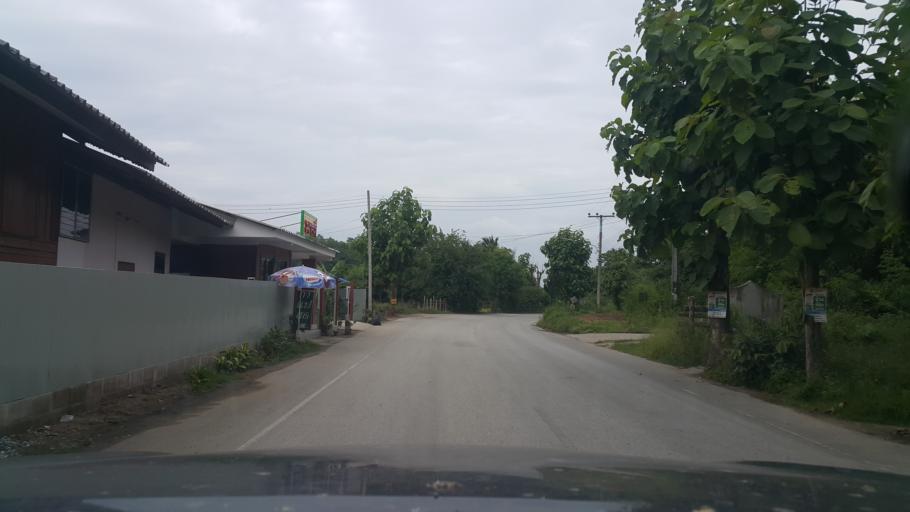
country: TH
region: Chiang Mai
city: San Pa Tong
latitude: 18.6651
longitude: 98.8357
